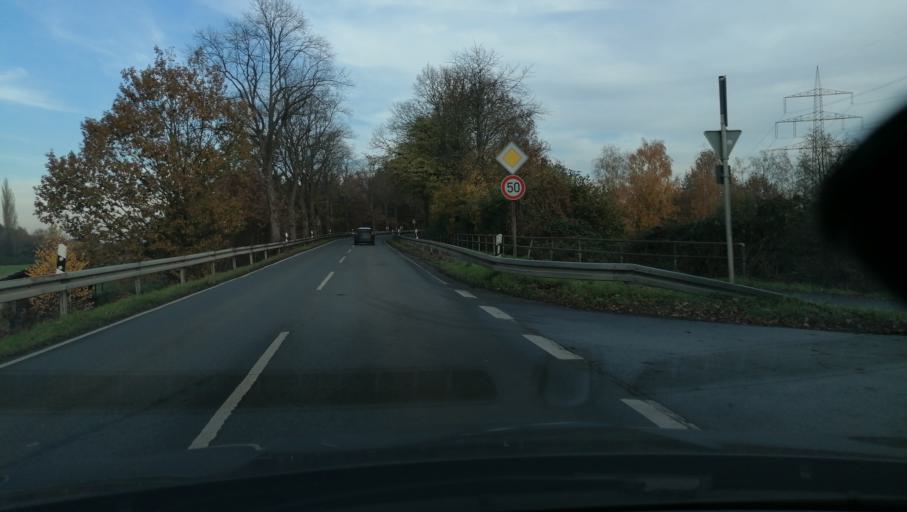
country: DE
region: North Rhine-Westphalia
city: Castrop-Rauxel
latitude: 51.5820
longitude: 7.2860
